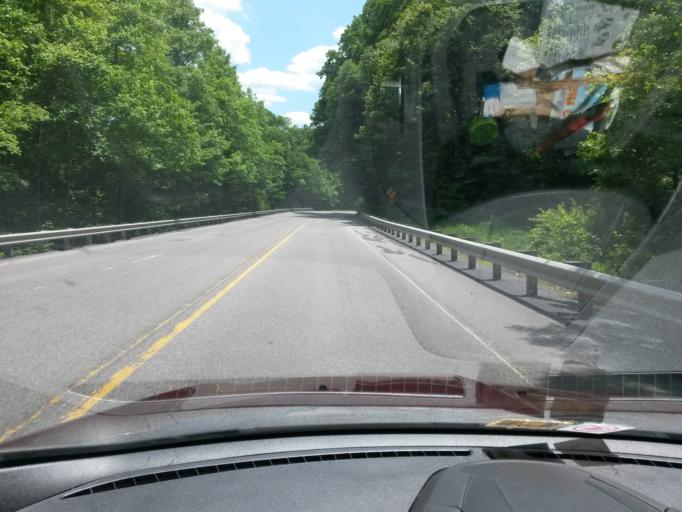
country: US
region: West Virginia
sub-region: Greenbrier County
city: Rainelle
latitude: 38.0190
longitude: -80.7252
